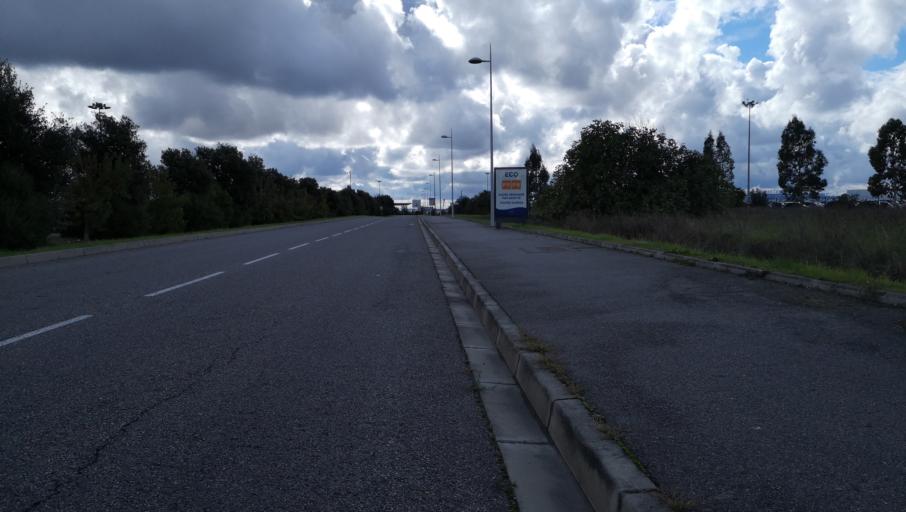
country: FR
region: Midi-Pyrenees
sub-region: Departement de la Haute-Garonne
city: Beauzelle
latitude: 43.6410
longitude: 1.3645
